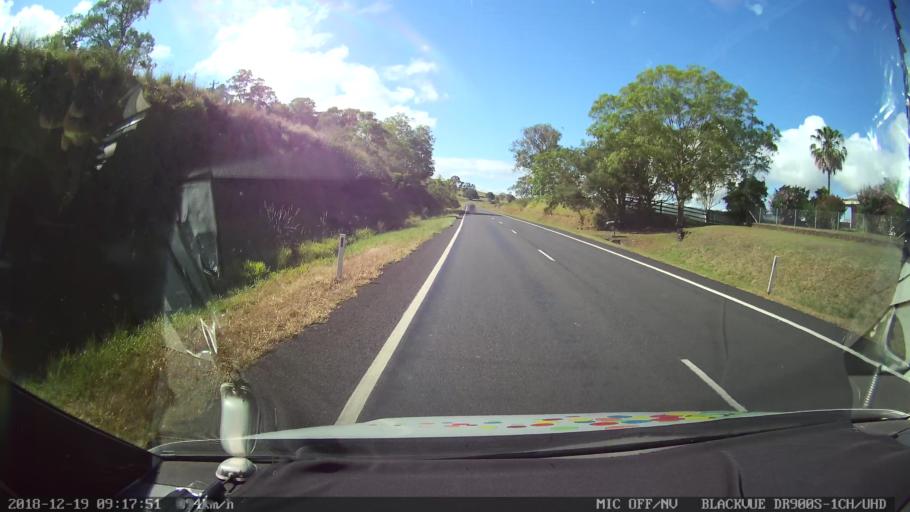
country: AU
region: New South Wales
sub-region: Kyogle
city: Kyogle
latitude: -28.5396
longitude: 152.9755
